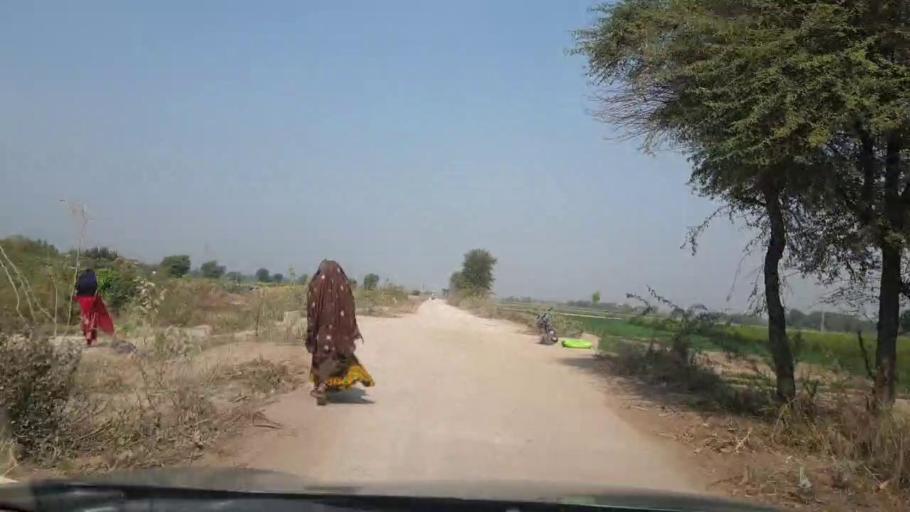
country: PK
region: Sindh
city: Tando Allahyar
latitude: 25.5031
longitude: 68.7960
